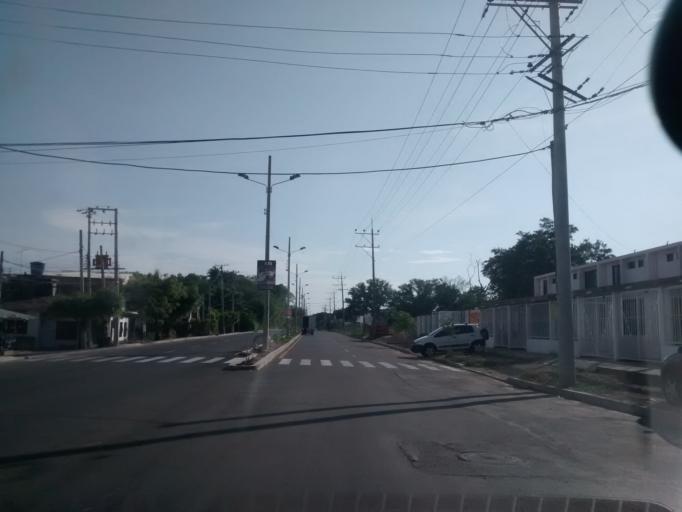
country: CO
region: Cundinamarca
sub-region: Girardot
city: Girardot City
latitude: 4.3103
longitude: -74.8103
